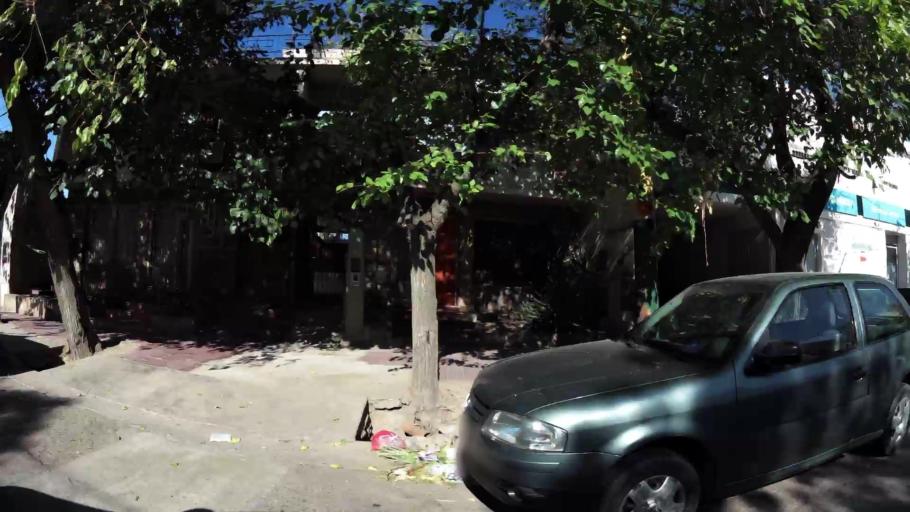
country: AR
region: Mendoza
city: Mendoza
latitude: -32.9074
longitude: -68.8315
